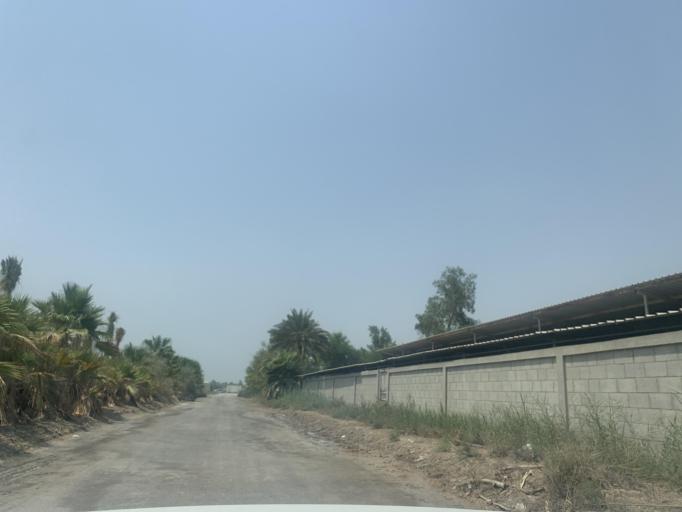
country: BH
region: Central Governorate
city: Madinat Hamad
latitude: 26.1233
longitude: 50.4663
